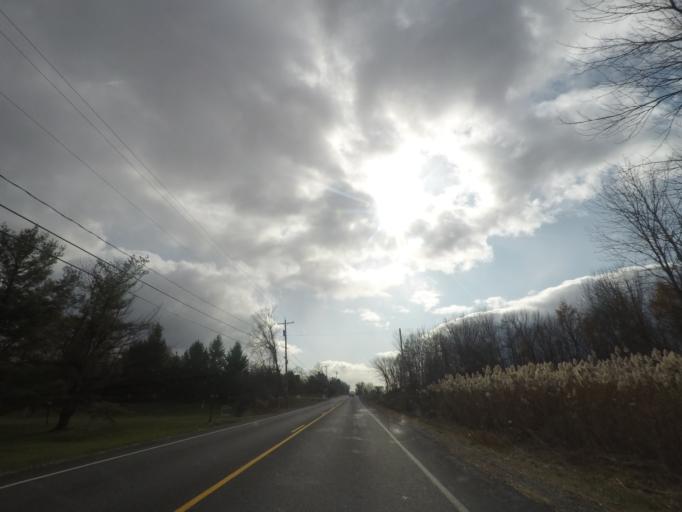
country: US
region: New York
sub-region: Saratoga County
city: Ballston Spa
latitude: 42.9653
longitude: -73.8300
